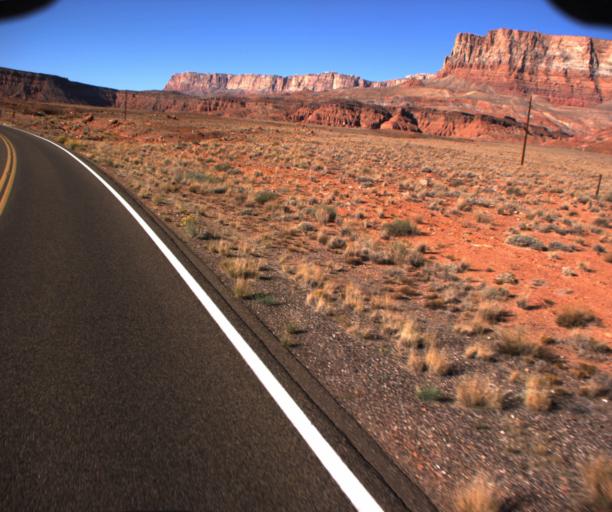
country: US
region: Arizona
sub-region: Coconino County
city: Page
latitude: 36.7791
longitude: -111.6937
